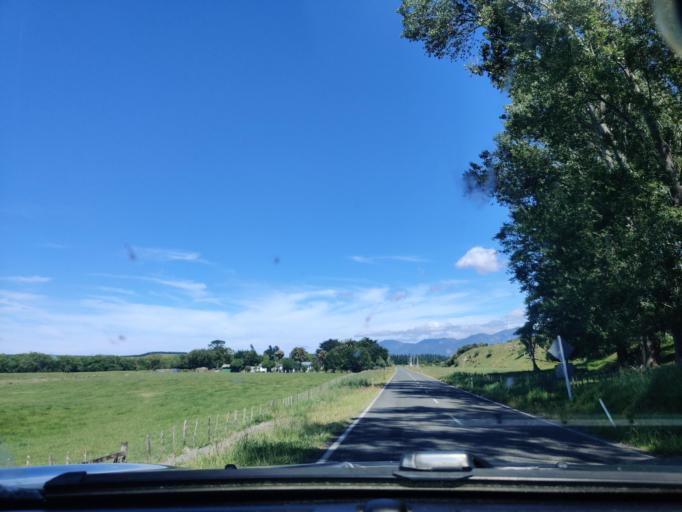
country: NZ
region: Wellington
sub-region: Upper Hutt City
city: Upper Hutt
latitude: -41.3666
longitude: 175.1948
